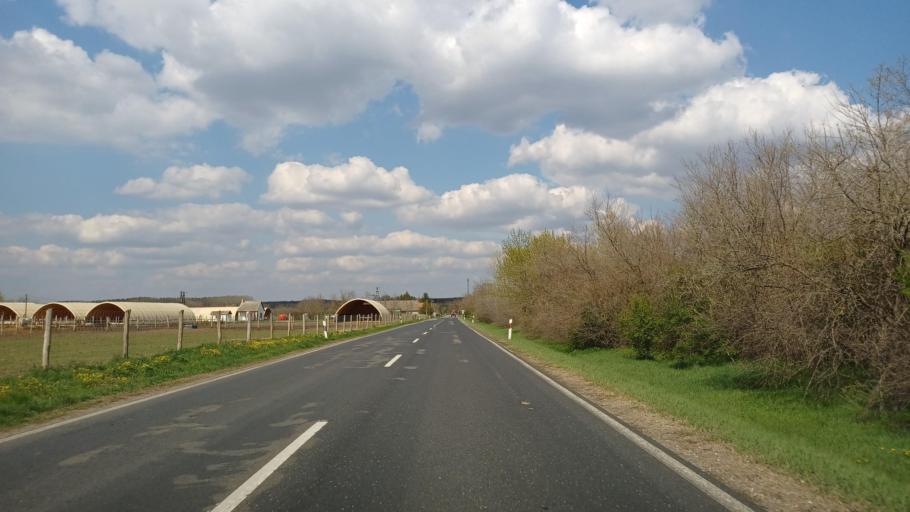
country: HU
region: Tolna
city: Nagydorog
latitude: 46.6704
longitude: 18.6604
